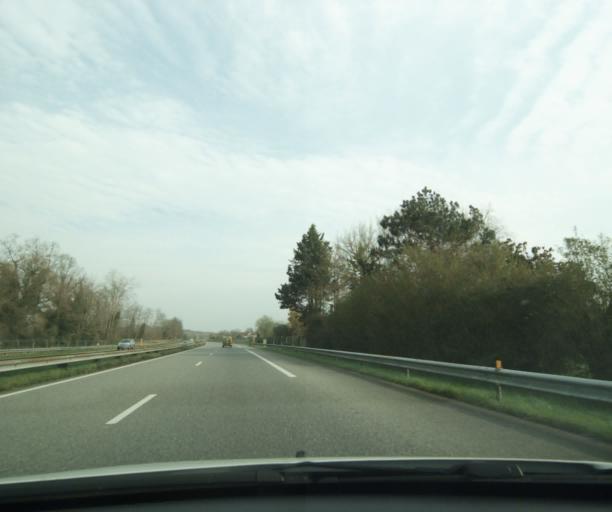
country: FR
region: Aquitaine
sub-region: Departement des Pyrenees-Atlantiques
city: Orthez
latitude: 43.4588
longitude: -0.7162
